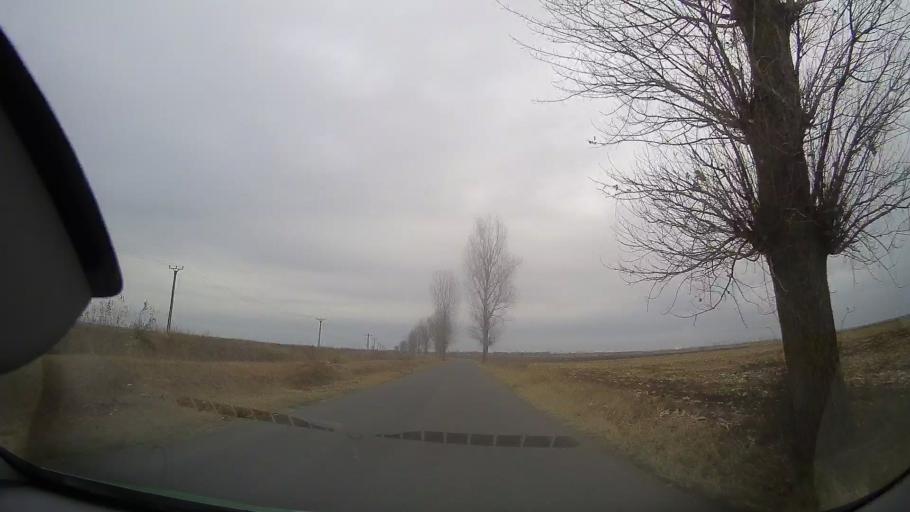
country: RO
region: Braila
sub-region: Comuna Rosiori
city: Rosiori
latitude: 44.8163
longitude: 27.3632
